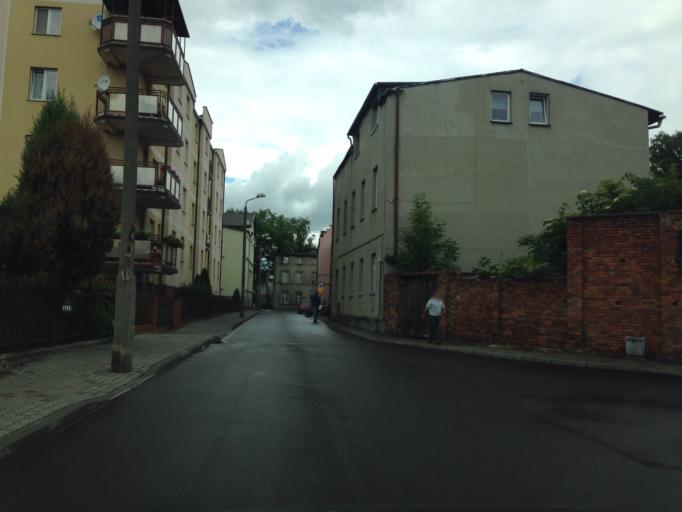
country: PL
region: Kujawsko-Pomorskie
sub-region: Powiat brodnicki
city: Brodnica
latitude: 53.2535
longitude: 19.4053
